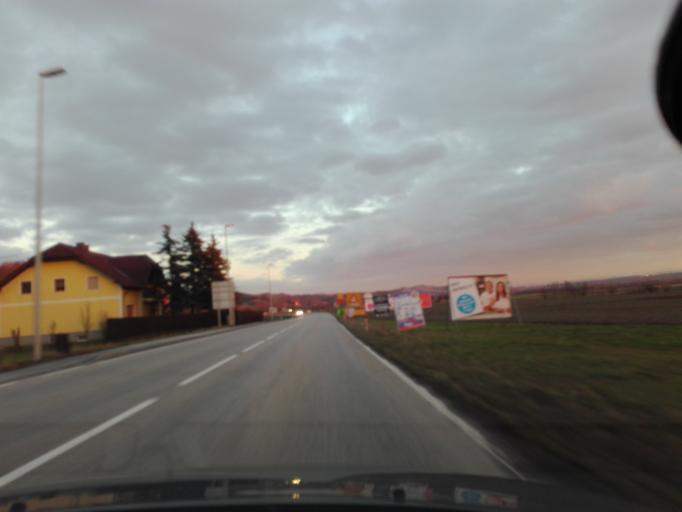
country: AT
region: Upper Austria
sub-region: Politischer Bezirk Perg
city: Bad Kreuzen
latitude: 48.2127
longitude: 14.7608
